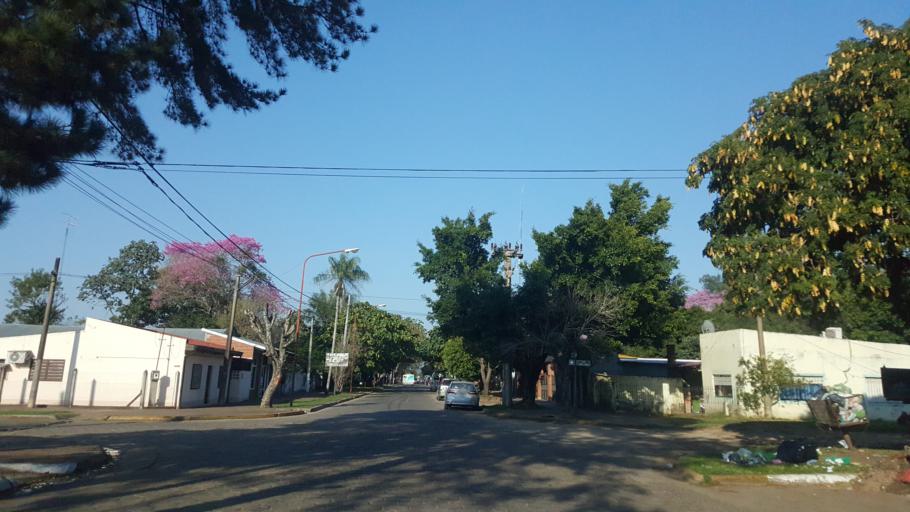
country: AR
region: Corrientes
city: Ituzaingo
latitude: -27.5815
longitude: -56.6839
